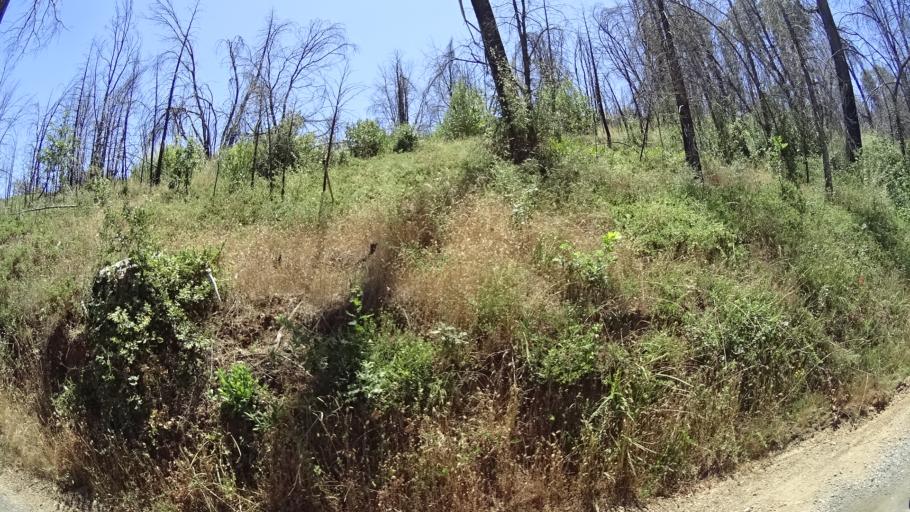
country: US
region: California
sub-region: Calaveras County
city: Mountain Ranch
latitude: 38.2434
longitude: -120.5768
